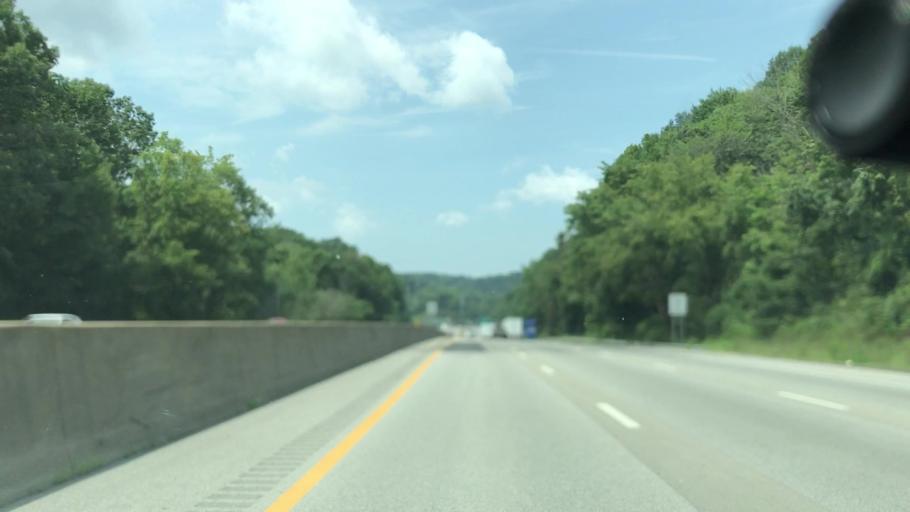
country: US
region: West Virginia
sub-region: Kanawha County
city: Cross Lanes
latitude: 38.3985
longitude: -81.7751
